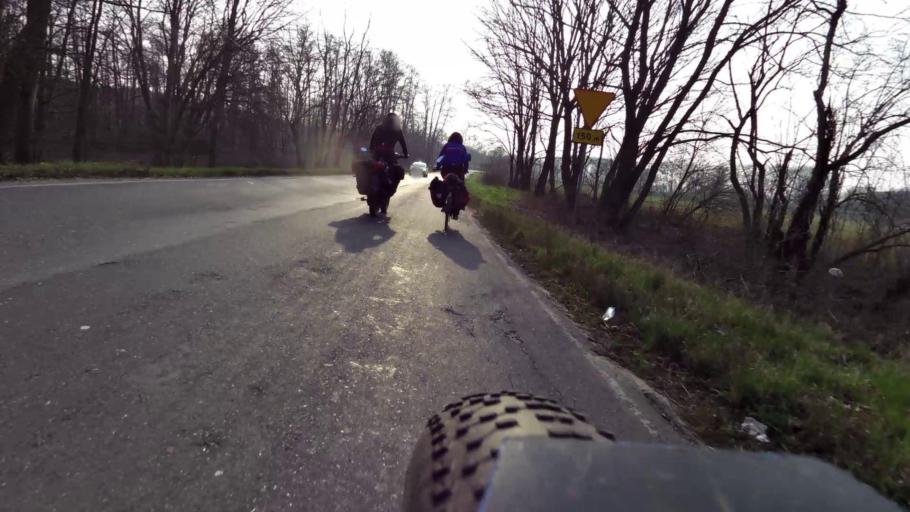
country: PL
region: Lubusz
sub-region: Powiat slubicki
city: Cybinka
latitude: 52.2508
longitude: 14.7343
